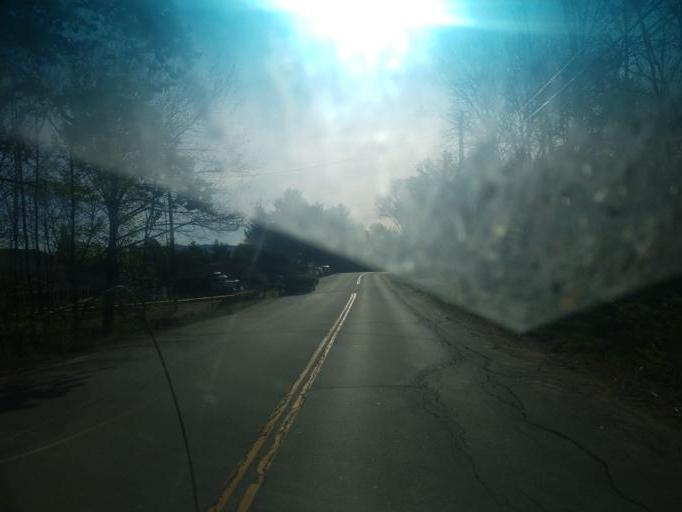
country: US
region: New Hampshire
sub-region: Grafton County
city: Deerfield
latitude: 44.2820
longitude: -71.6555
